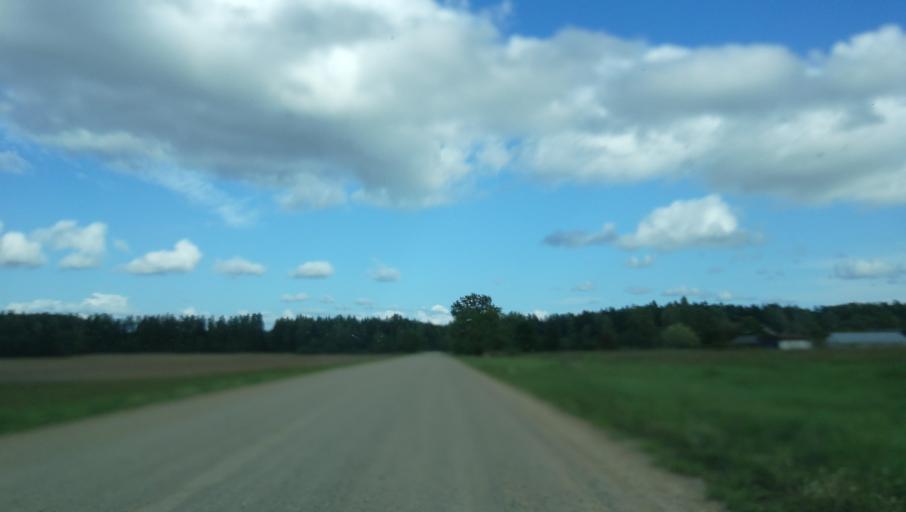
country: LV
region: Malpils
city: Malpils
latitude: 56.9616
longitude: 24.9426
